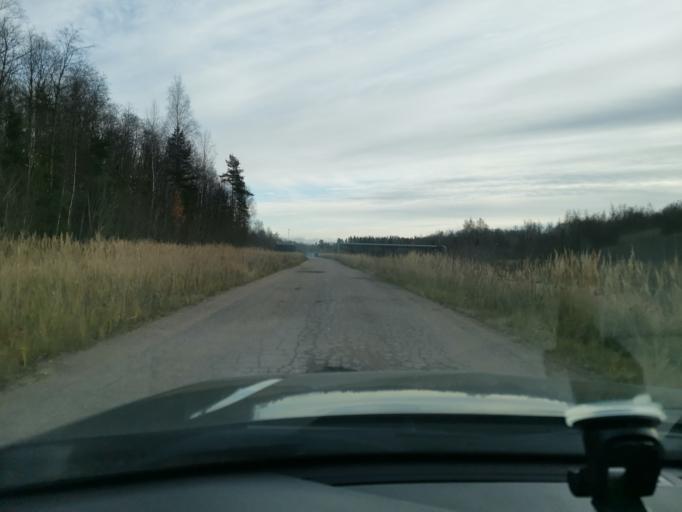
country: EE
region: Ida-Virumaa
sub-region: Sillamaee linn
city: Sillamae
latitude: 59.2618
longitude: 27.9068
